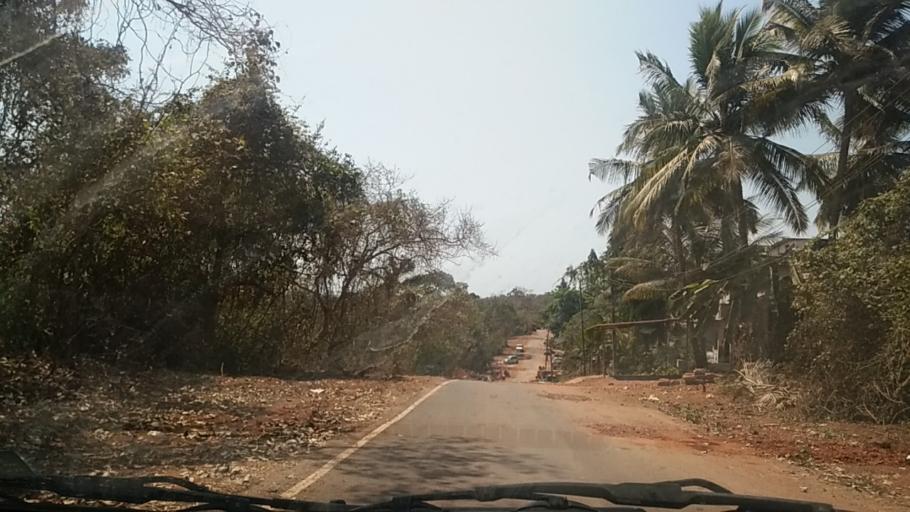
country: IN
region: Goa
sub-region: North Goa
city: Panaji
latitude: 15.5158
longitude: 73.8390
